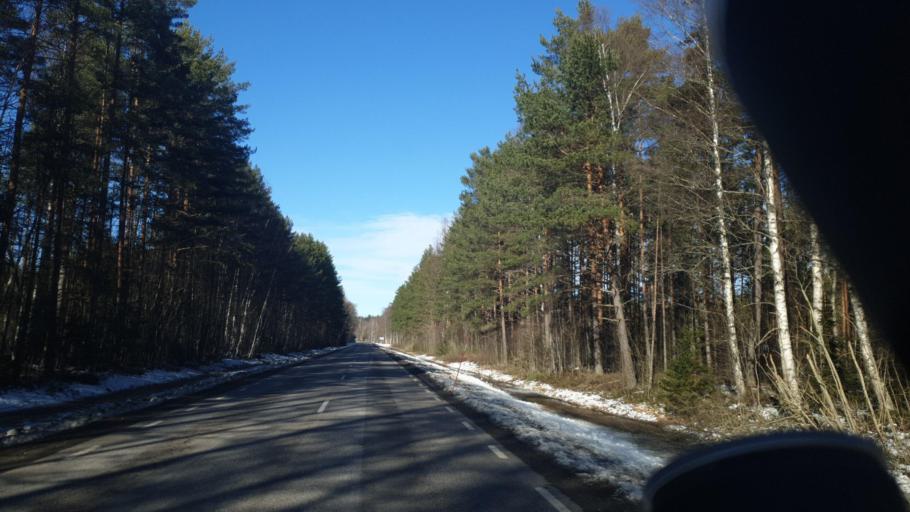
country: SE
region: Vaermland
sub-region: Arvika Kommun
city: Arvika
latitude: 59.6547
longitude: 12.8890
